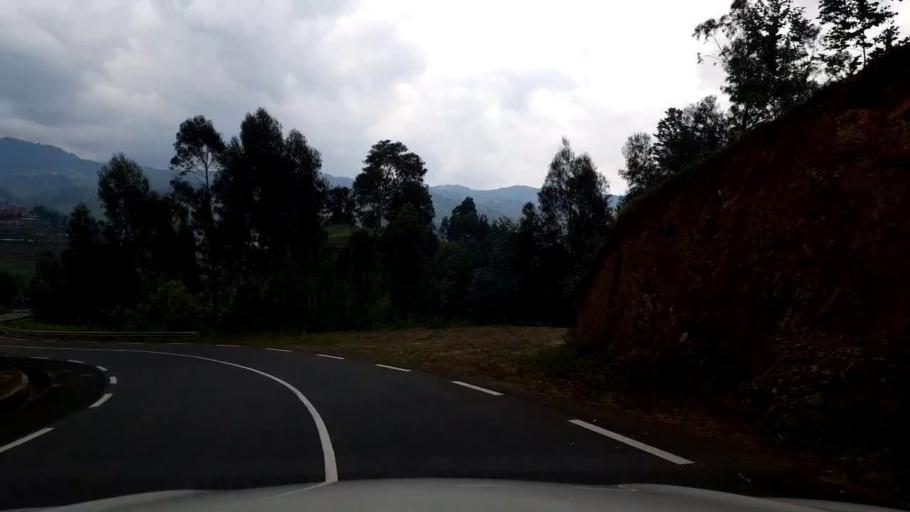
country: RW
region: Western Province
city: Kibuye
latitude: -1.9047
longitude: 29.3635
